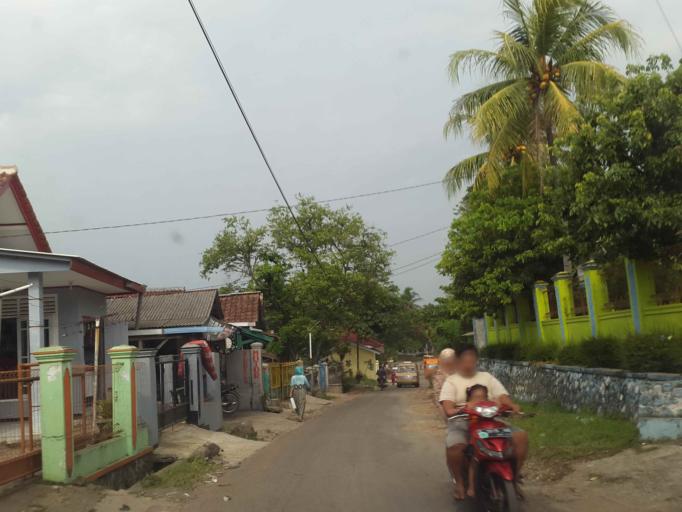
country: ID
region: West Java
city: Ciranjang-hilir
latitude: -6.7181
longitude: 107.2406
